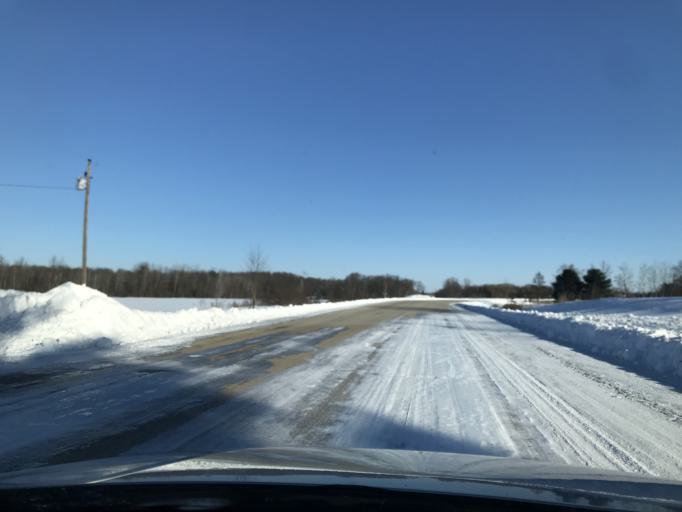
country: US
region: Wisconsin
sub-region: Oconto County
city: Oconto Falls
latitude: 44.9669
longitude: -88.0461
